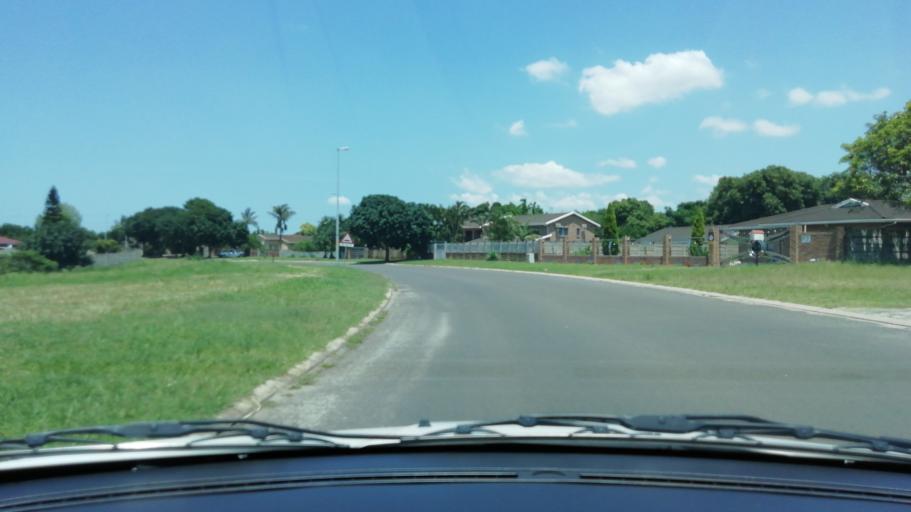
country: ZA
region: KwaZulu-Natal
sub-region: uThungulu District Municipality
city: Richards Bay
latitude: -28.7332
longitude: 32.0465
